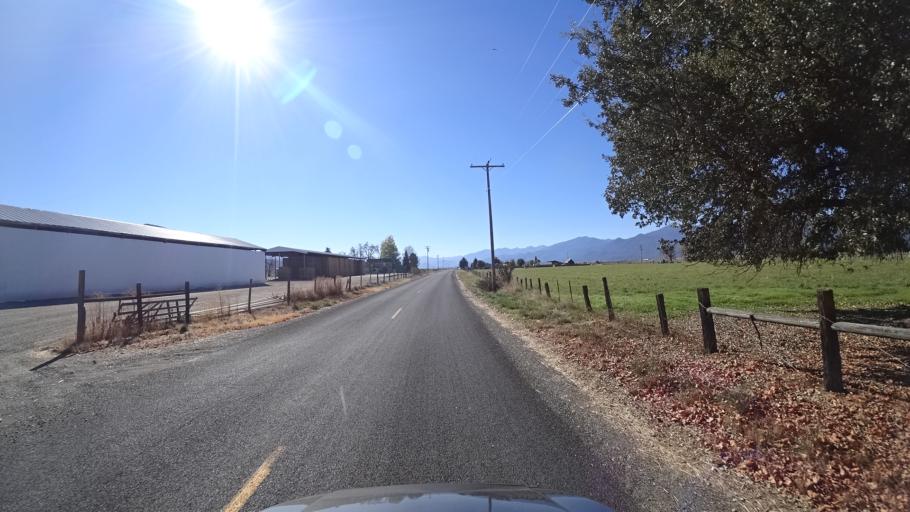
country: US
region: California
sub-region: Siskiyou County
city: Yreka
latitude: 41.5484
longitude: -122.8526
